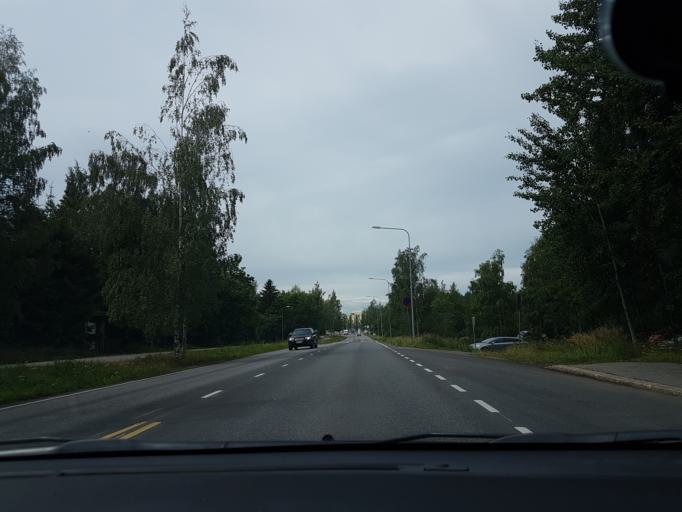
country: FI
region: Uusimaa
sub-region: Helsinki
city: Vantaa
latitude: 60.2559
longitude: 25.0318
